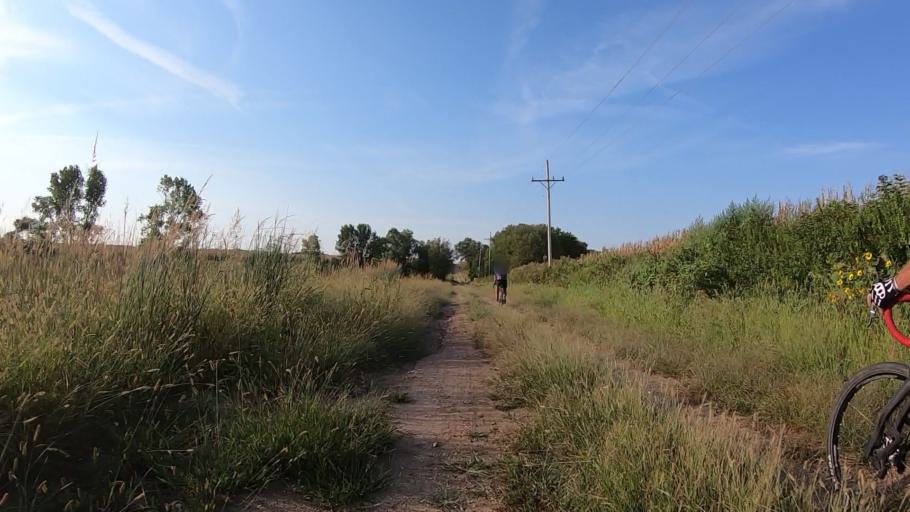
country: US
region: Kansas
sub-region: Marshall County
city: Blue Rapids
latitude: 39.7059
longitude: -96.7792
